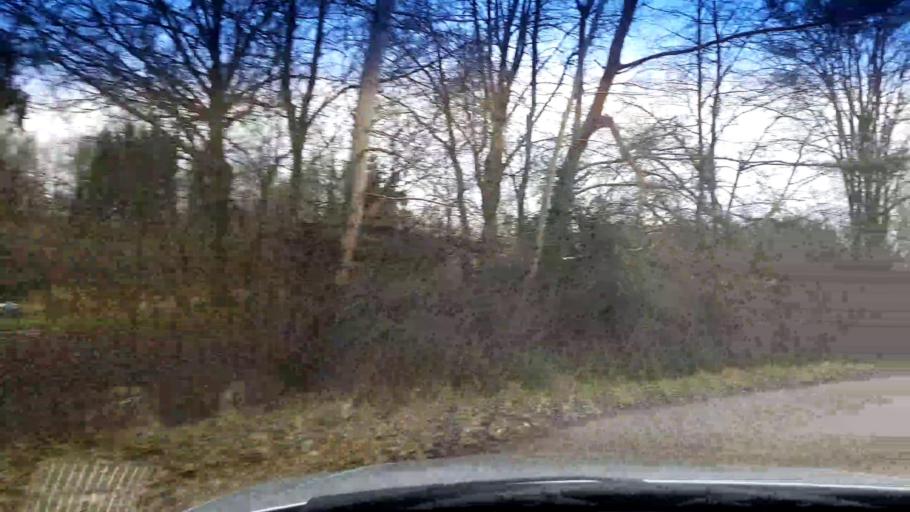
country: DE
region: Bavaria
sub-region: Upper Franconia
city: Baunach
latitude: 49.9798
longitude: 10.8360
